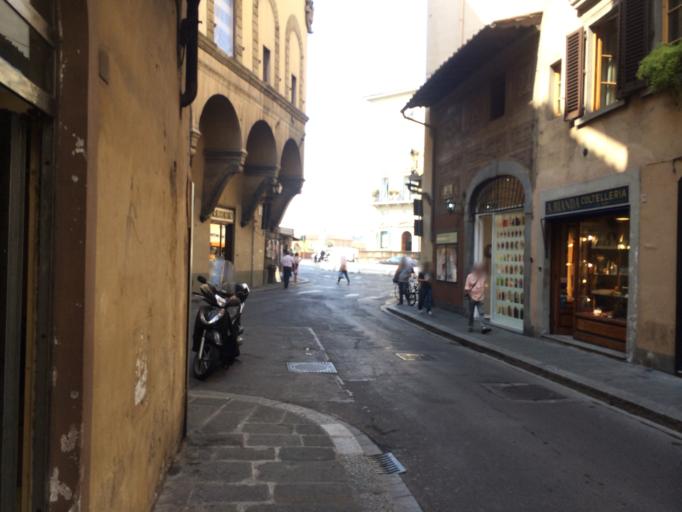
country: IT
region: Tuscany
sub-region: Province of Florence
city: Florence
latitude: 43.7710
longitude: 11.2484
